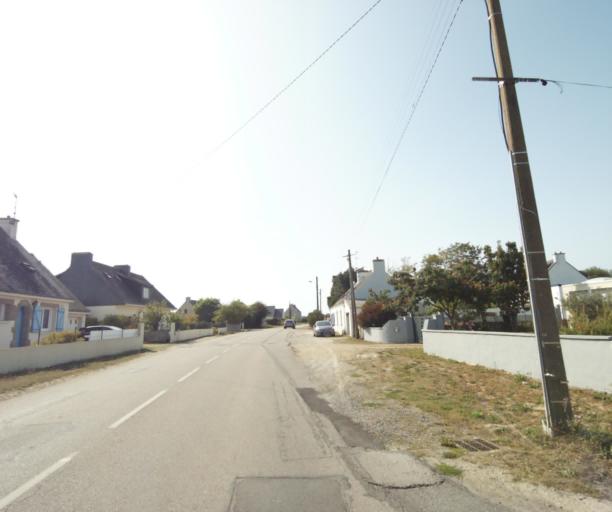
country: FR
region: Brittany
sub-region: Departement du Morbihan
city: Riantec
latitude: 47.7099
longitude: -3.2929
